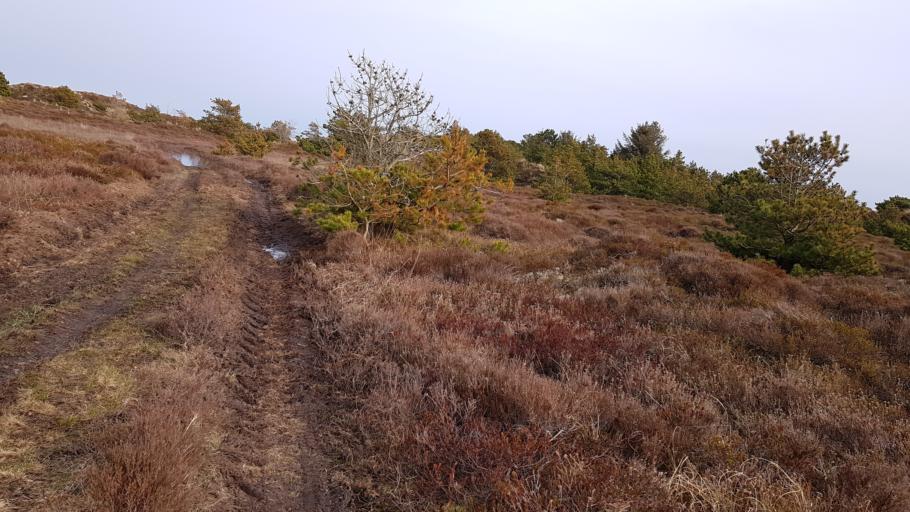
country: DE
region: Schleswig-Holstein
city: List
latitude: 55.1625
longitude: 8.5233
